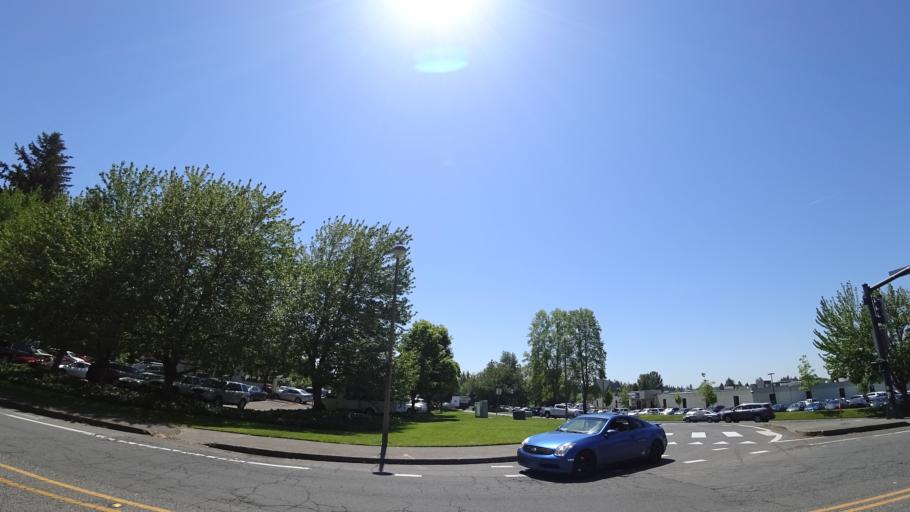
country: US
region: Oregon
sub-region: Washington County
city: Beaverton
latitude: 45.4944
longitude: -122.8258
